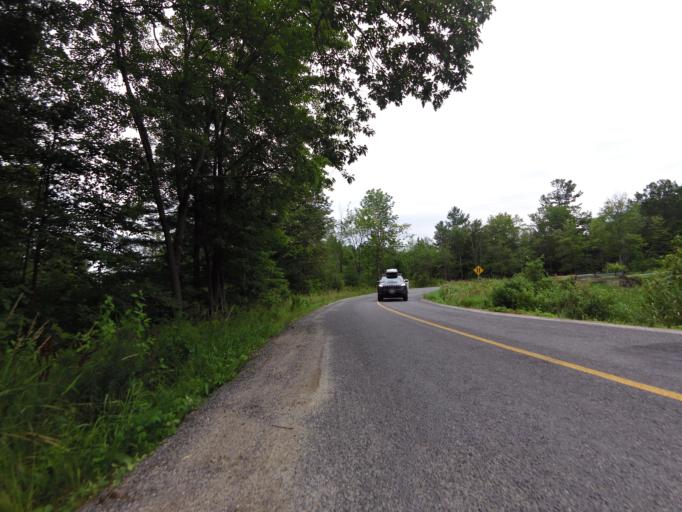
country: CA
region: Ontario
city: Kingston
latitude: 44.6601
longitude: -76.6558
